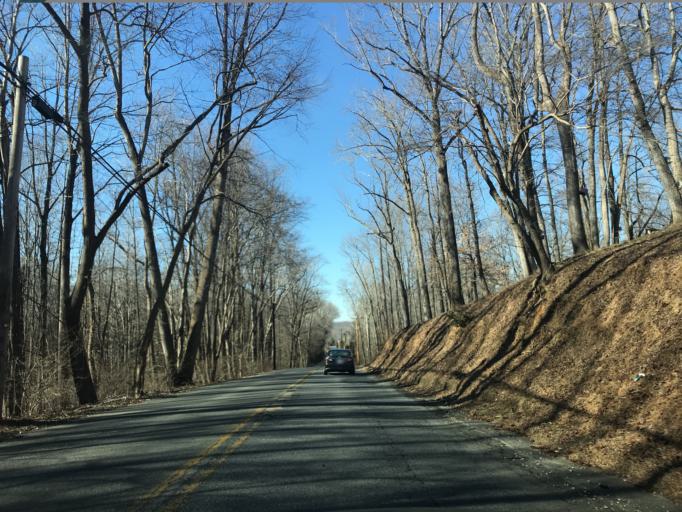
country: US
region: Maryland
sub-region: Charles County
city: Bennsville
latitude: 38.5844
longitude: -77.0436
